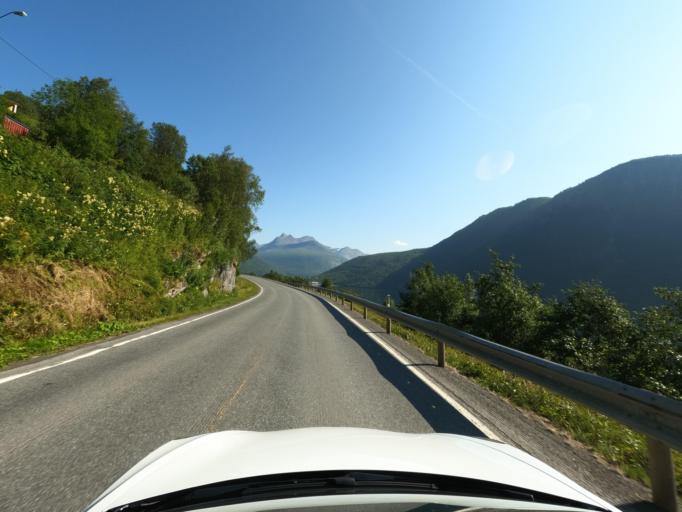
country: NO
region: Nordland
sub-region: Narvik
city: Narvik
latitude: 68.3887
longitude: 17.5500
